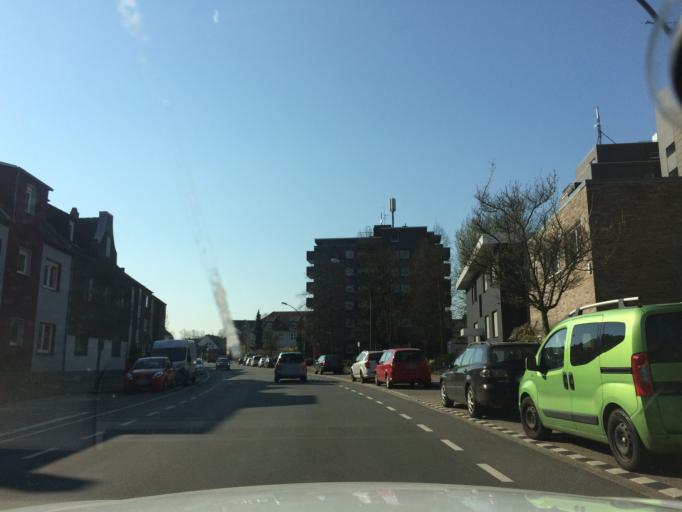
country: DE
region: North Rhine-Westphalia
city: Herten
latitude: 51.6025
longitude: 7.0912
